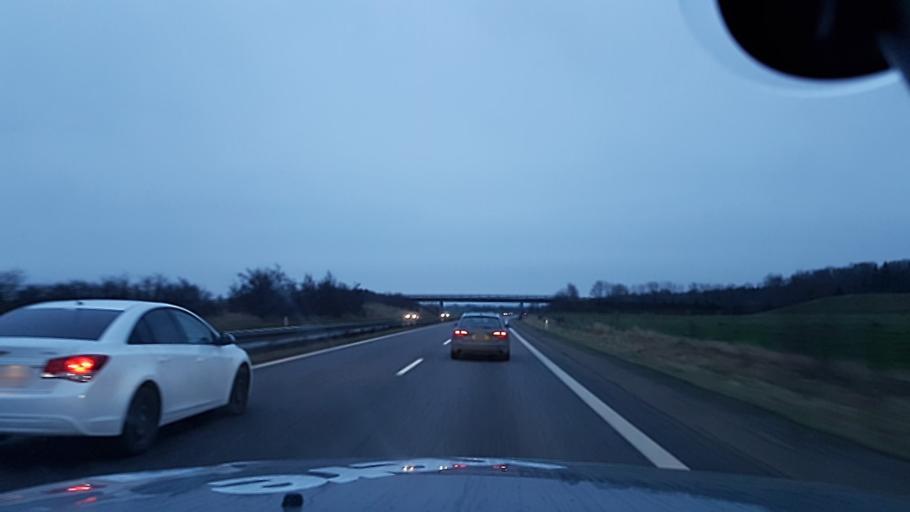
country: DK
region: Zealand
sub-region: Faxe Kommune
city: Ronnede
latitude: 55.2076
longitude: 11.9763
